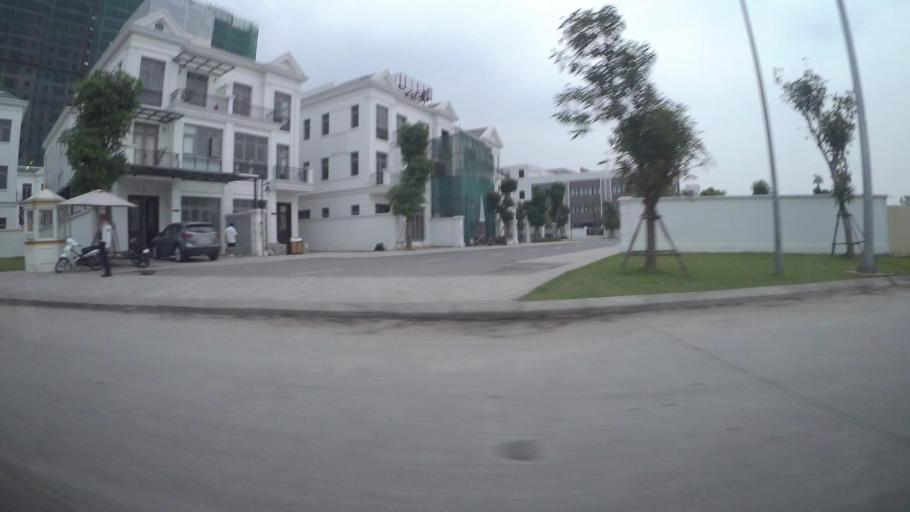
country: VN
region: Ha Noi
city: Trau Quy
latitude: 21.0428
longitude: 105.9055
